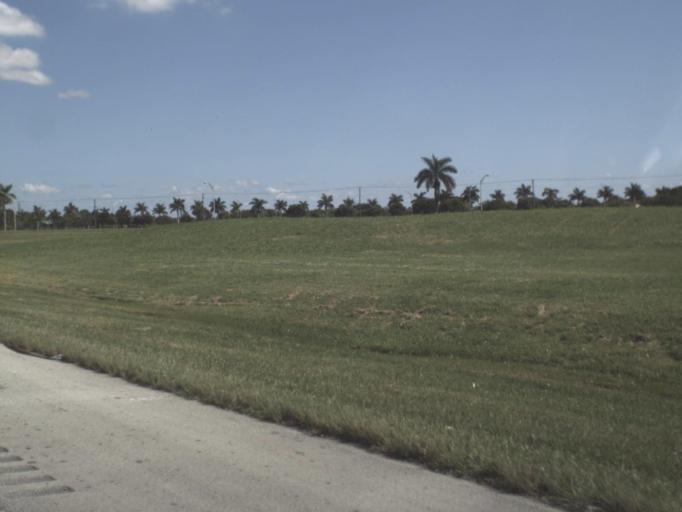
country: US
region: Florida
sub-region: Miami-Dade County
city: Naranja
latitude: 25.5072
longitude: -80.4157
